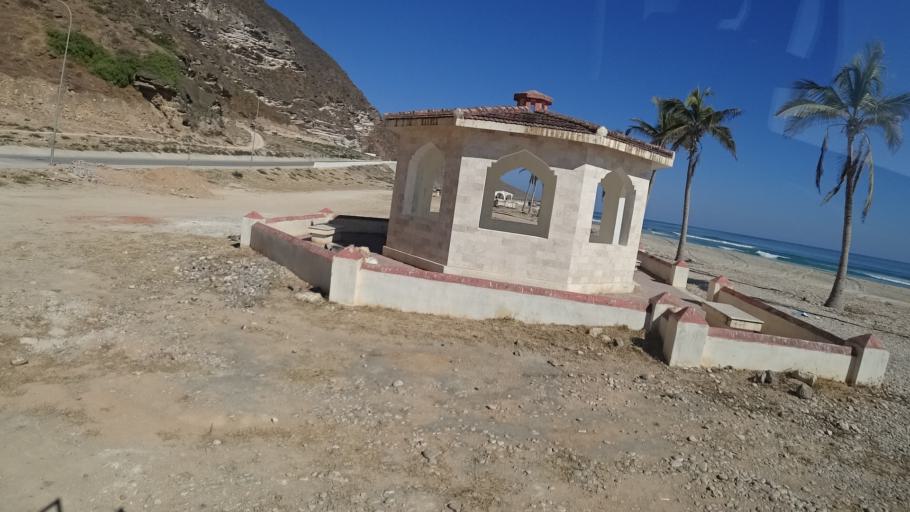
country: YE
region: Al Mahrah
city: Hawf
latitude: 16.7474
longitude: 53.4296
